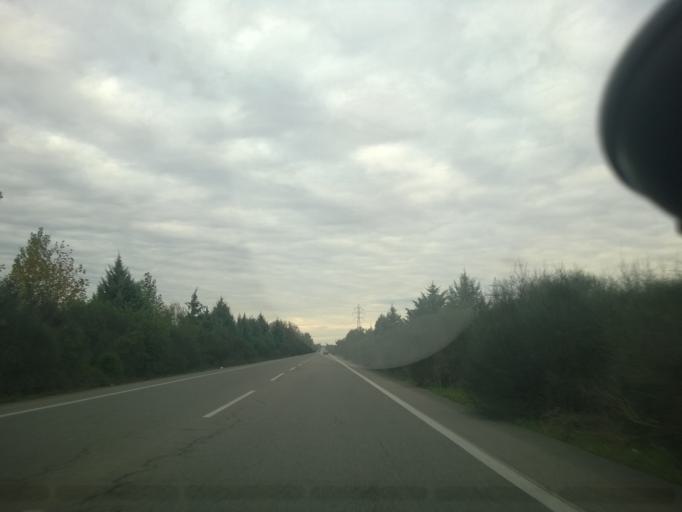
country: GR
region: Central Macedonia
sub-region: Nomos Pellis
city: Melissi
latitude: 40.7779
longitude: 22.3435
